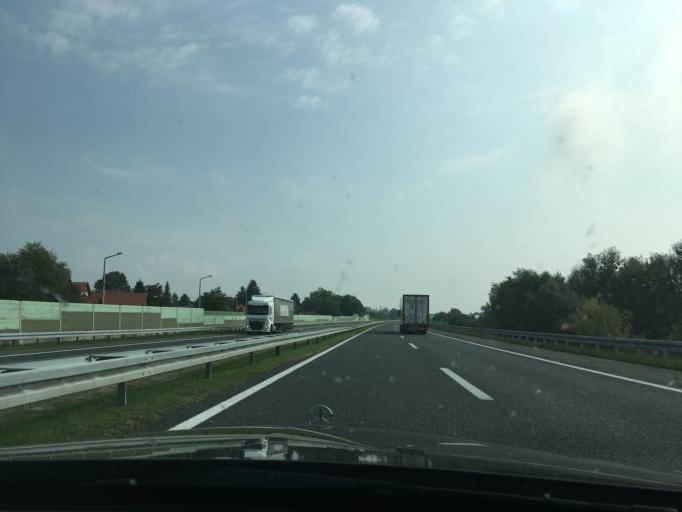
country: HR
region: Brodsko-Posavska
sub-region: Grad Slavonski Brod
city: Slavonski Brod
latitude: 45.1802
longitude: 17.9815
